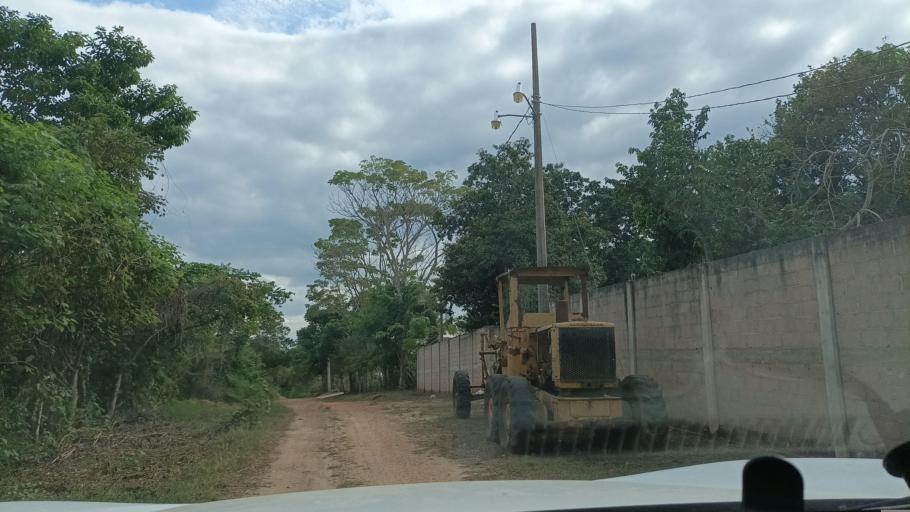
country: MX
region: Veracruz
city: Oluta
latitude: 17.9416
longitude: -94.8822
